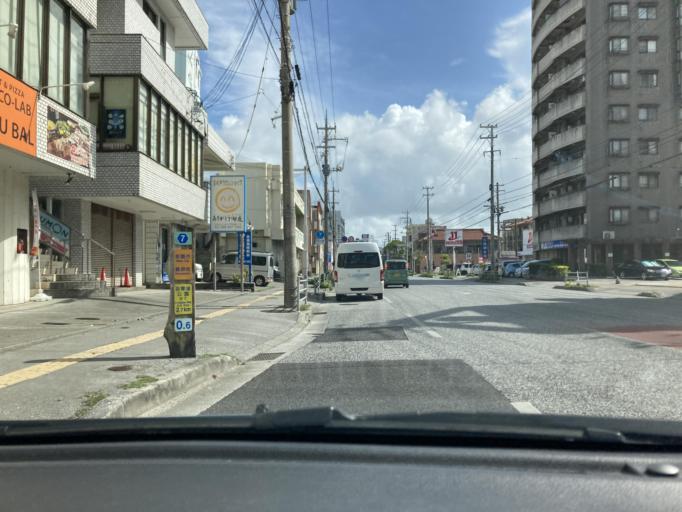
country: JP
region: Okinawa
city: Naha-shi
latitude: 26.2003
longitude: 127.6750
